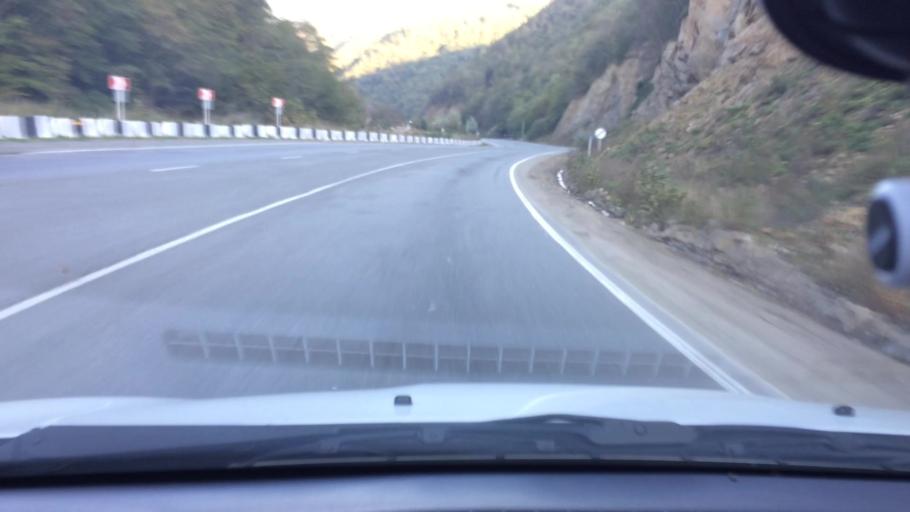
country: GE
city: Surami
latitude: 42.0851
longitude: 43.4678
